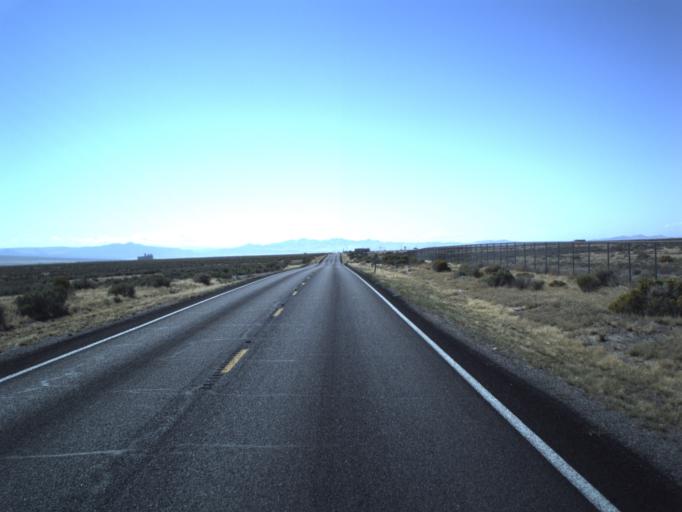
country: US
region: Utah
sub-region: Beaver County
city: Milford
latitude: 38.4340
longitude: -113.0098
